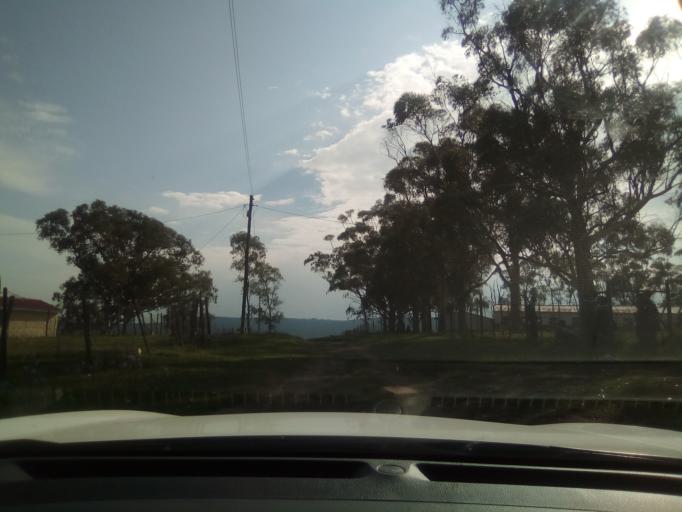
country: ZA
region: Eastern Cape
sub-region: Buffalo City Metropolitan Municipality
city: Bhisho
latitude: -32.9855
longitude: 27.2591
